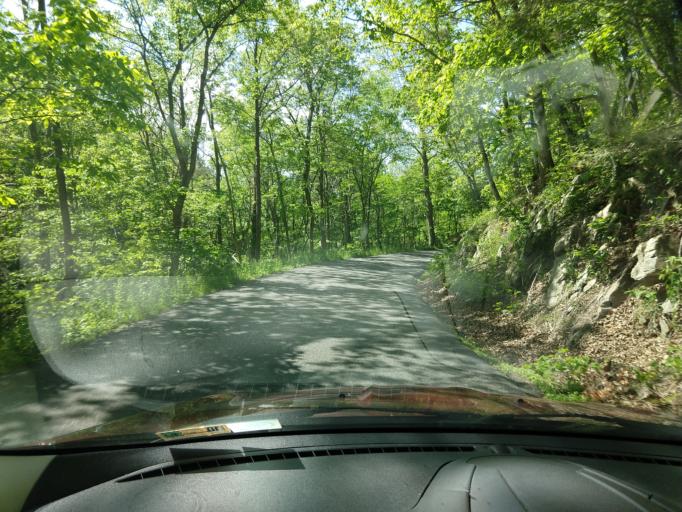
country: US
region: Virginia
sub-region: City of Covington
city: Fairlawn
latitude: 37.7124
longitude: -79.9109
